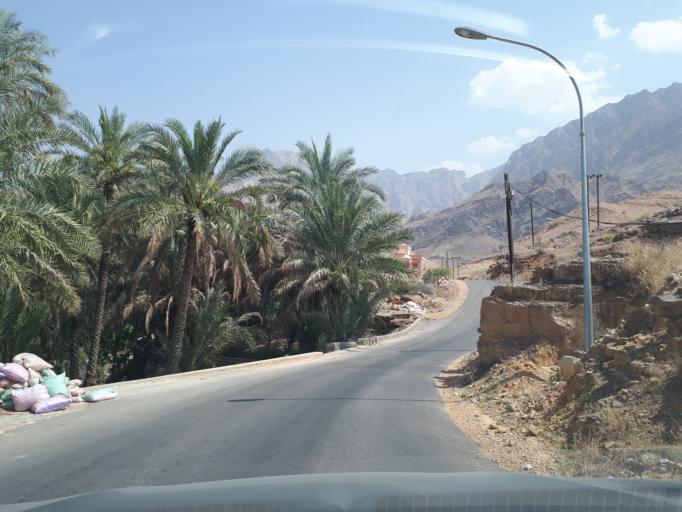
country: OM
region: Ash Sharqiyah
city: Ibra'
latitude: 23.0836
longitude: 58.8658
